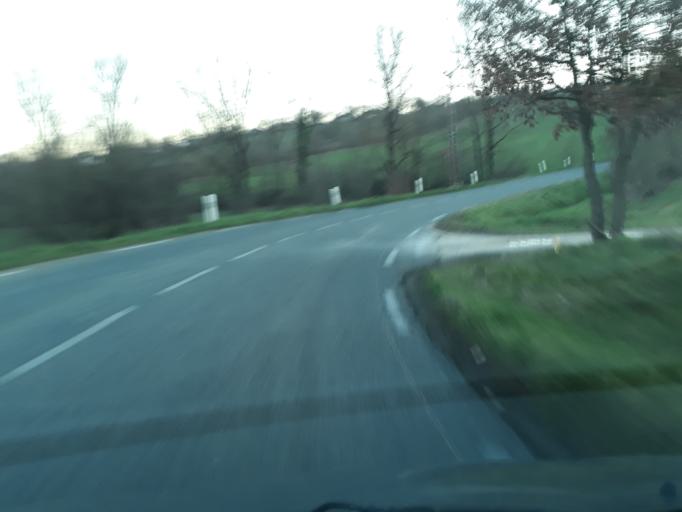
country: FR
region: Midi-Pyrenees
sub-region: Departement du Gers
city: Pujaudran
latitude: 43.5688
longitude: 1.1331
